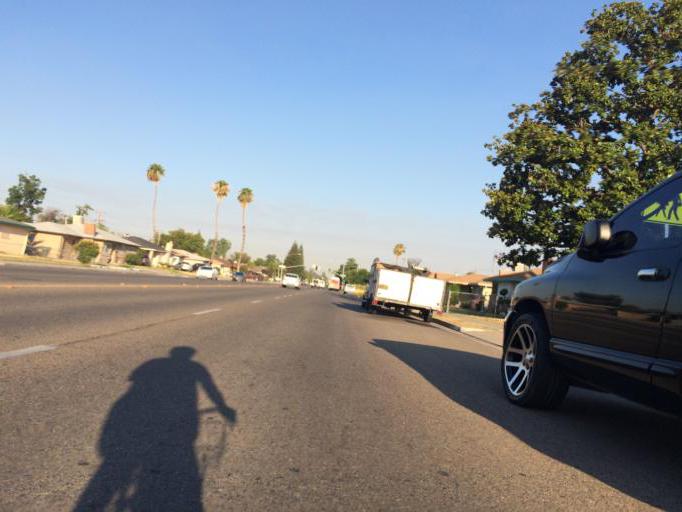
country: US
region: California
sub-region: Fresno County
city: Fresno
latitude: 36.7723
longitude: -119.7384
